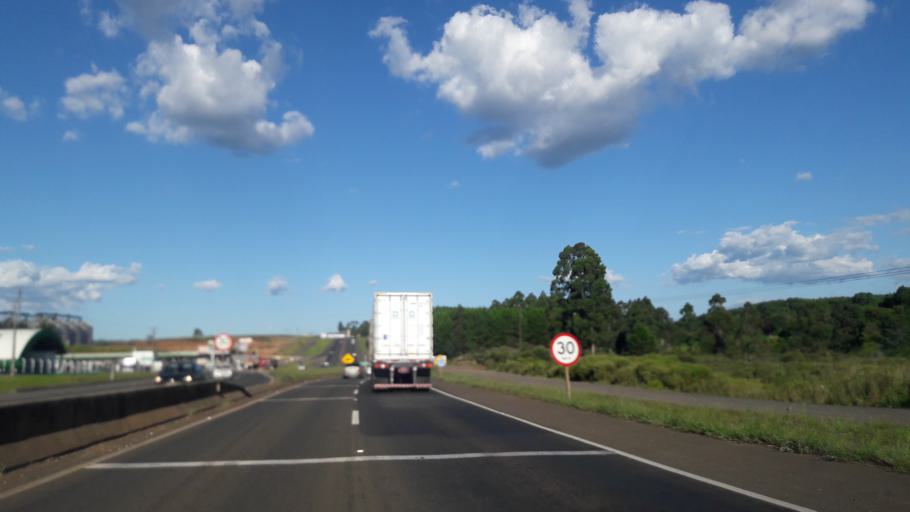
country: BR
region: Parana
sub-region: Guarapuava
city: Guarapuava
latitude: -25.3454
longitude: -51.4441
